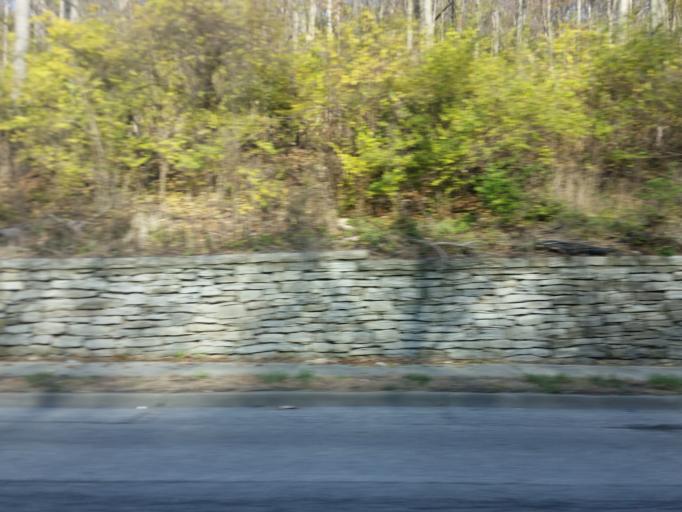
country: US
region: Ohio
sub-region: Hamilton County
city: Monfort Heights
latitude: 39.1694
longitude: -84.5577
